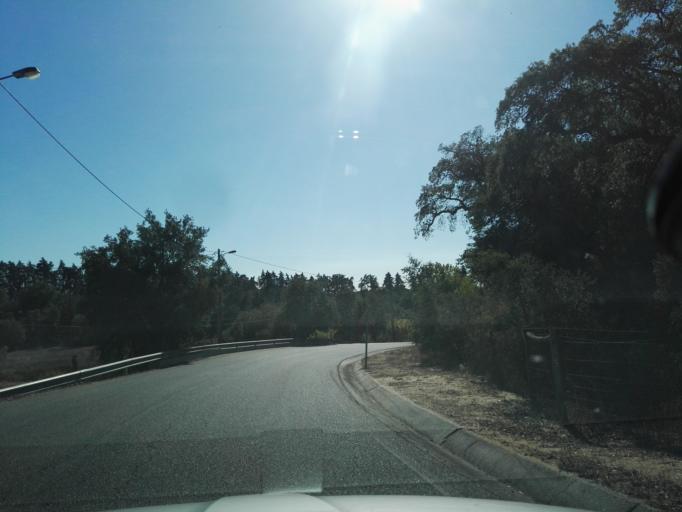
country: PT
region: Santarem
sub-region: Benavente
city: Poceirao
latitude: 38.8690
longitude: -8.7476
